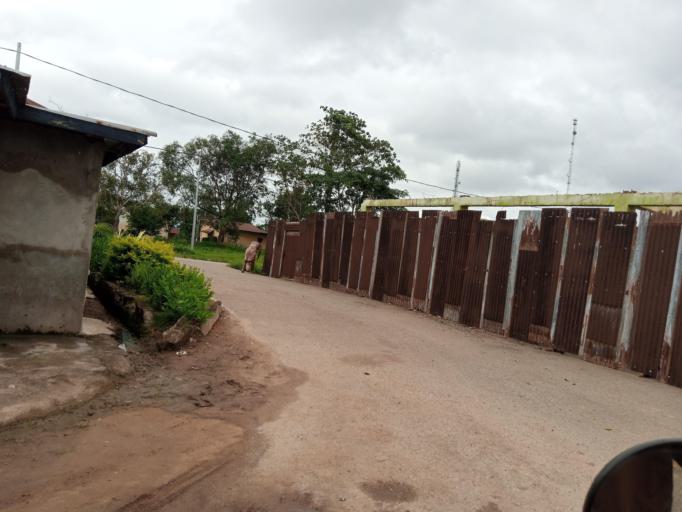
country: SL
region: Southern Province
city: Largo
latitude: 8.1963
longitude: -12.0579
